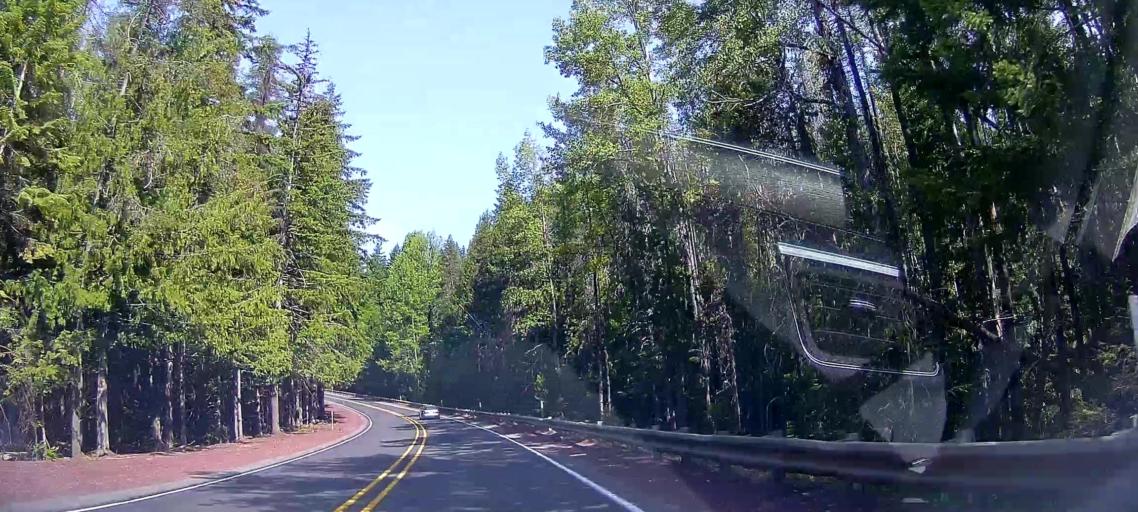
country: US
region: Oregon
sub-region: Clackamas County
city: Mount Hood Village
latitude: 45.1252
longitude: -121.5882
